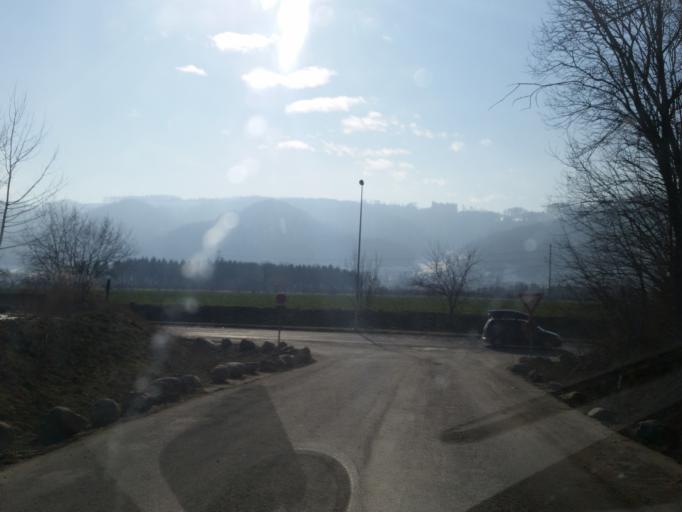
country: CH
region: Aargau
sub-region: Bezirk Baden
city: Neuenhof
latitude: 47.4538
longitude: 8.3406
